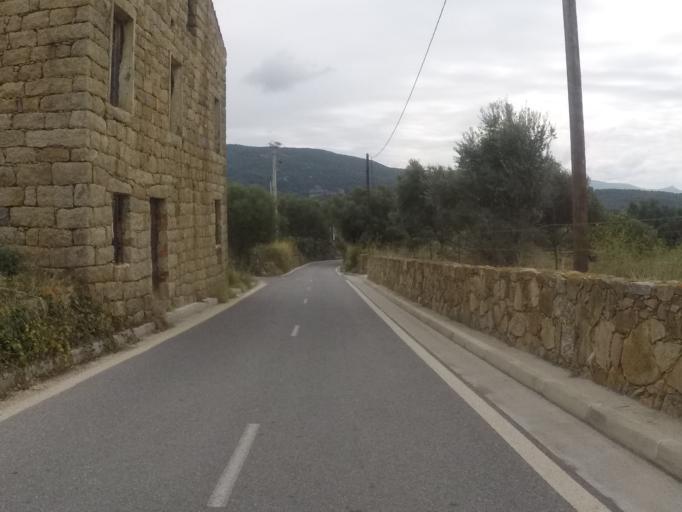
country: FR
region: Corsica
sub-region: Departement de la Corse-du-Sud
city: Olmeto
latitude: 41.7300
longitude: 8.8283
